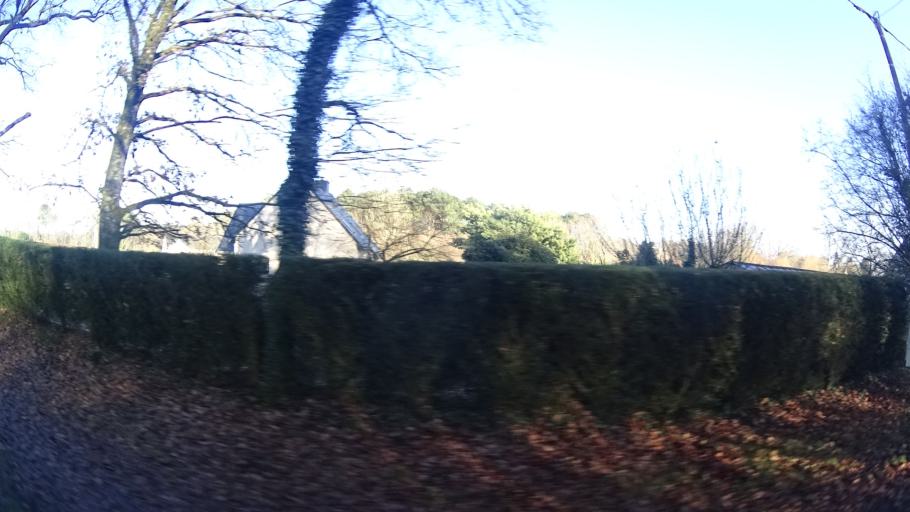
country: FR
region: Brittany
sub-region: Departement du Morbihan
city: Allaire
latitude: 47.6432
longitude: -2.1764
